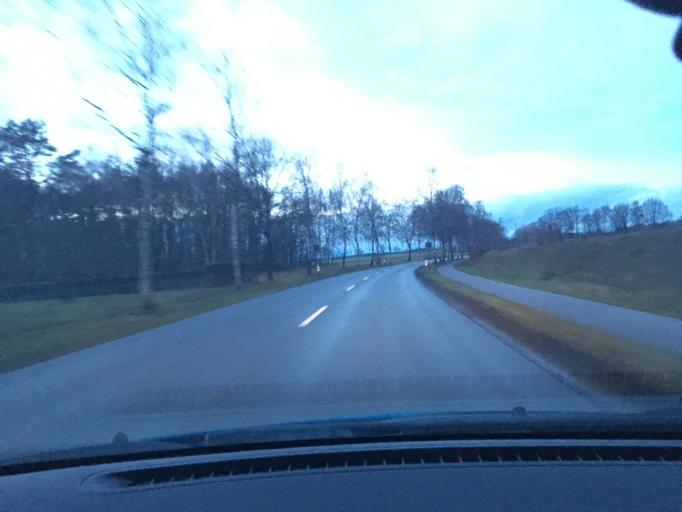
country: DE
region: Lower Saxony
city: Embsen
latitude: 53.1810
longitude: 10.3350
